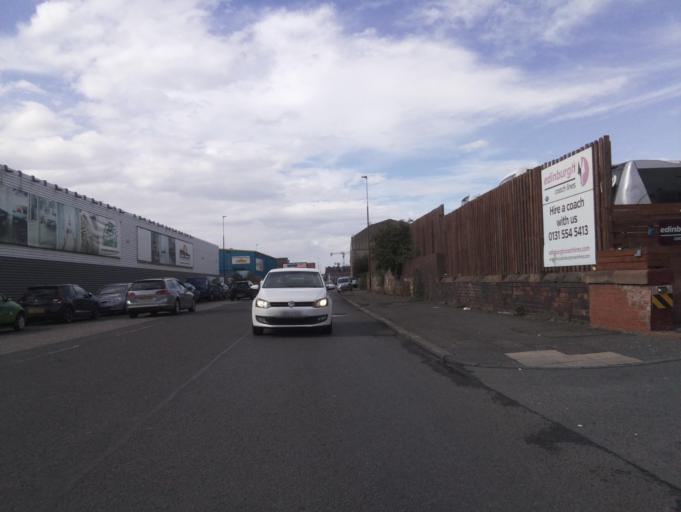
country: GB
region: Scotland
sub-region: West Lothian
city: Seafield
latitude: 55.9720
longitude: -3.1530
